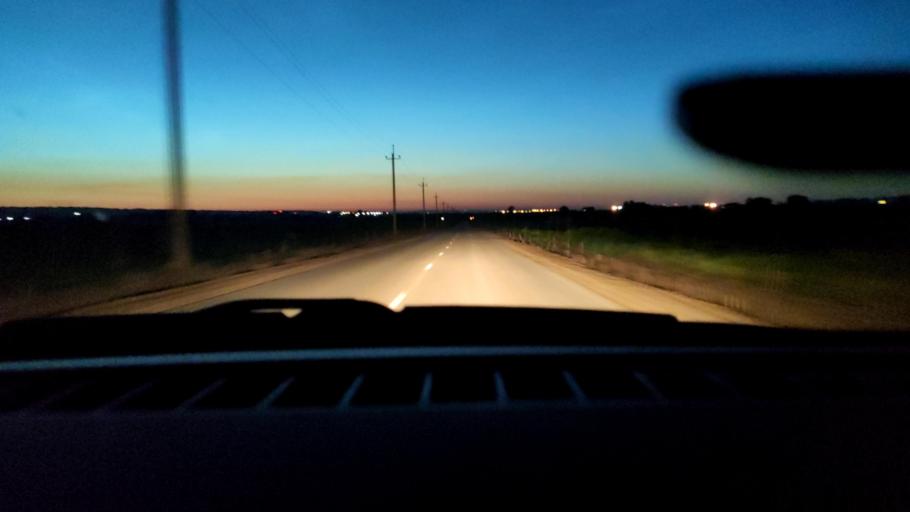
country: RU
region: Perm
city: Kultayevo
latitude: 57.8888
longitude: 55.9901
